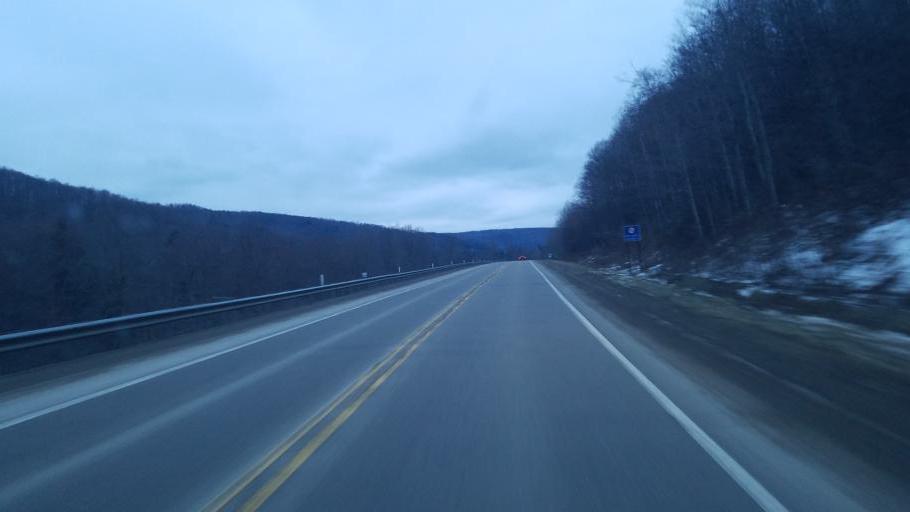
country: US
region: Pennsylvania
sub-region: Potter County
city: Coudersport
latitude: 41.7985
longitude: -78.0150
